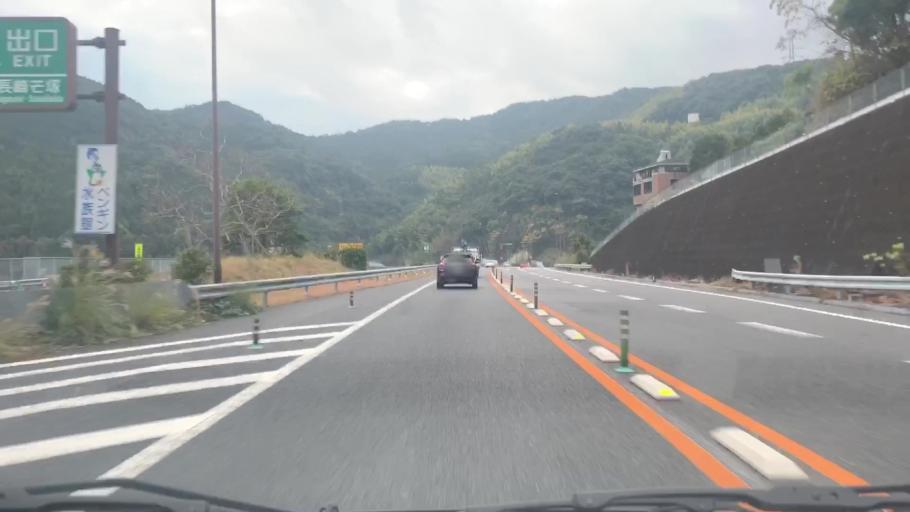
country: JP
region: Nagasaki
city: Nagasaki-shi
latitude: 32.7544
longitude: 129.9284
